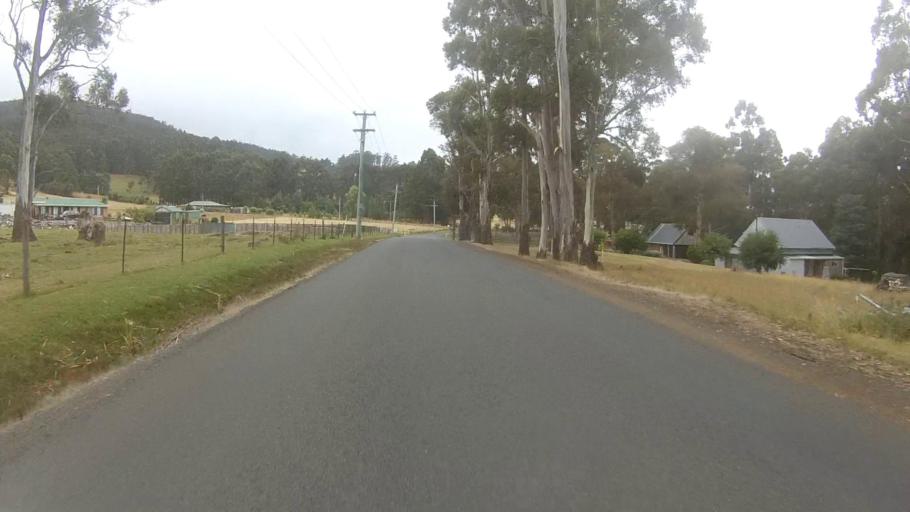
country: AU
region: Tasmania
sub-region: Kingborough
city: Margate
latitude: -42.9609
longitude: 147.2198
